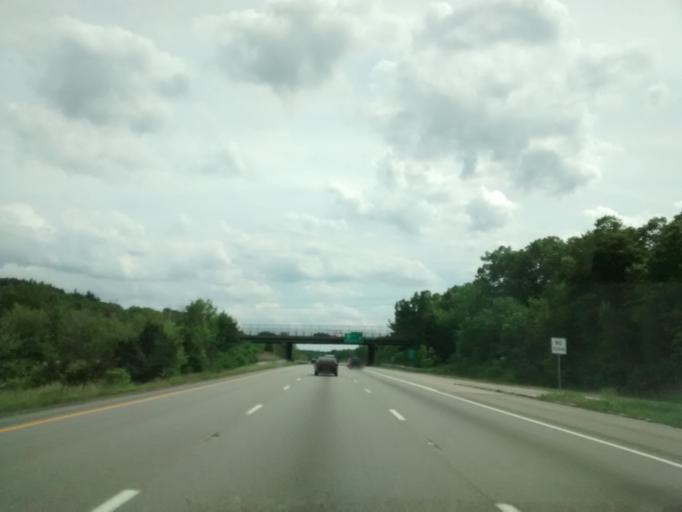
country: US
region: Massachusetts
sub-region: Middlesex County
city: Marlborough
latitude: 42.3429
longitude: -71.5755
